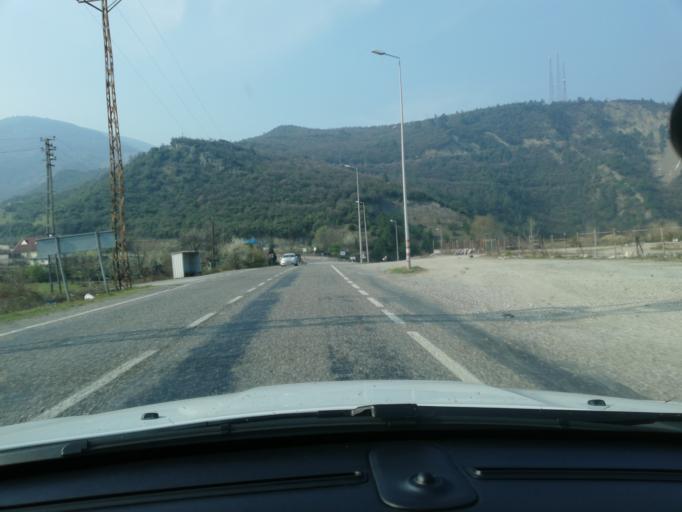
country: TR
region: Karabuk
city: Karabuk
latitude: 41.1533
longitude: 32.5350
